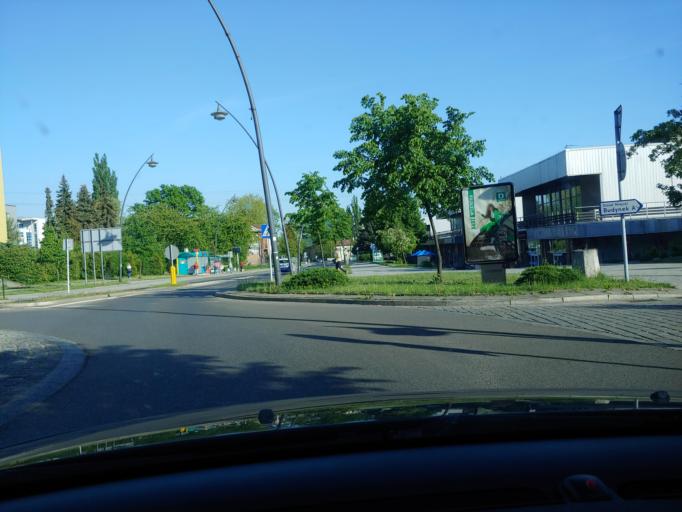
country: PL
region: Silesian Voivodeship
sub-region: Jaworzno
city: Jaworzno
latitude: 50.1996
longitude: 19.2758
